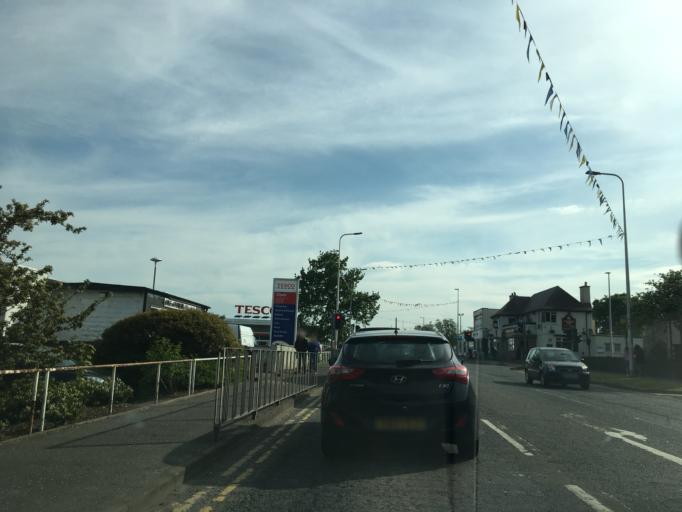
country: GB
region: Scotland
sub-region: Midlothian
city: Penicuik
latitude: 55.8364
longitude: -3.2199
